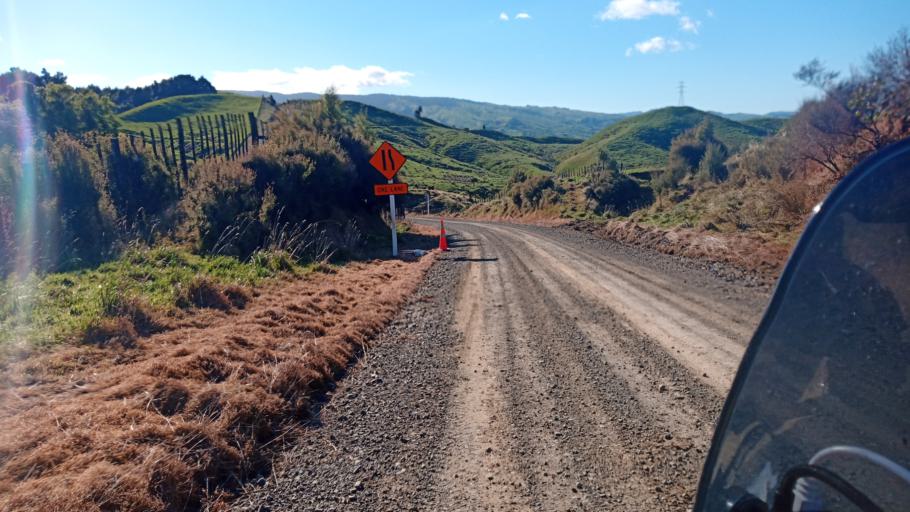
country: NZ
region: Hawke's Bay
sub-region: Wairoa District
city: Wairoa
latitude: -38.7559
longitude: 177.2653
